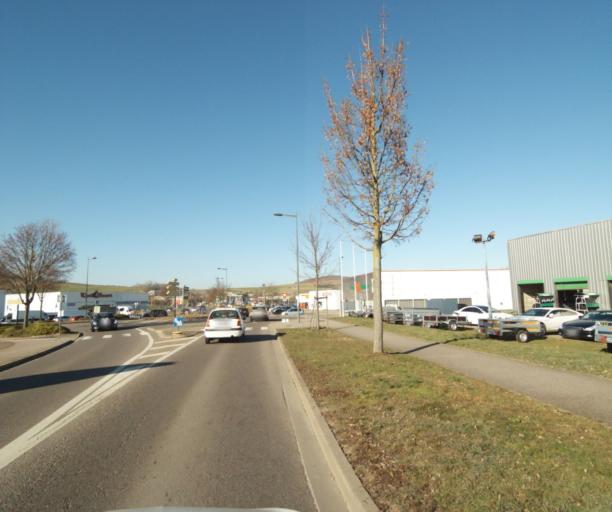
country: FR
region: Lorraine
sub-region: Departement de Meurthe-et-Moselle
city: Pulnoy
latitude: 48.7058
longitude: 6.2454
